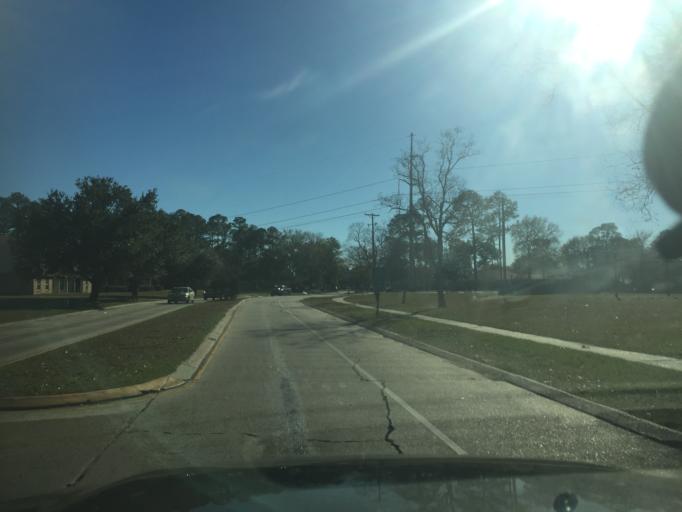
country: US
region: Louisiana
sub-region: Saint Tammany Parish
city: Slidell
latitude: 30.2916
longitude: -89.7581
